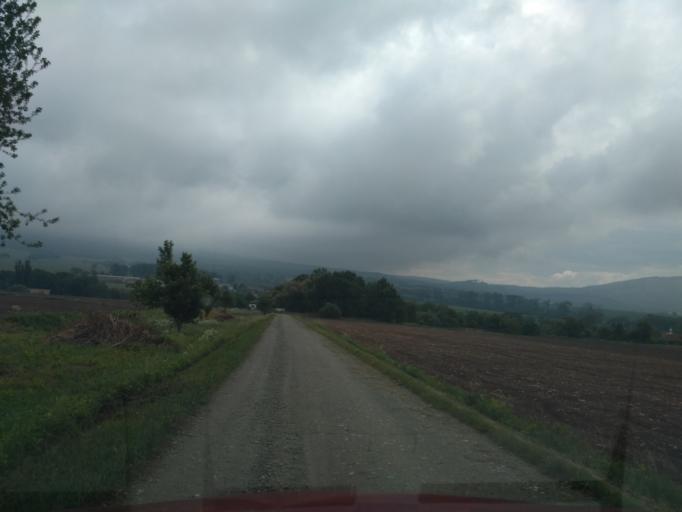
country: SK
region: Kosicky
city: Secovce
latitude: 48.7652
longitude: 21.4751
